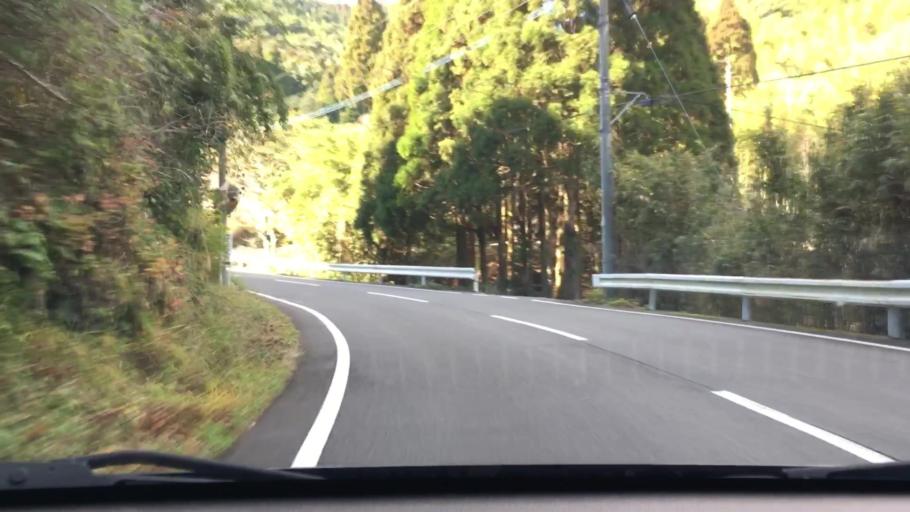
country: JP
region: Kagoshima
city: Ijuin
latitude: 31.7178
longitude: 130.4294
